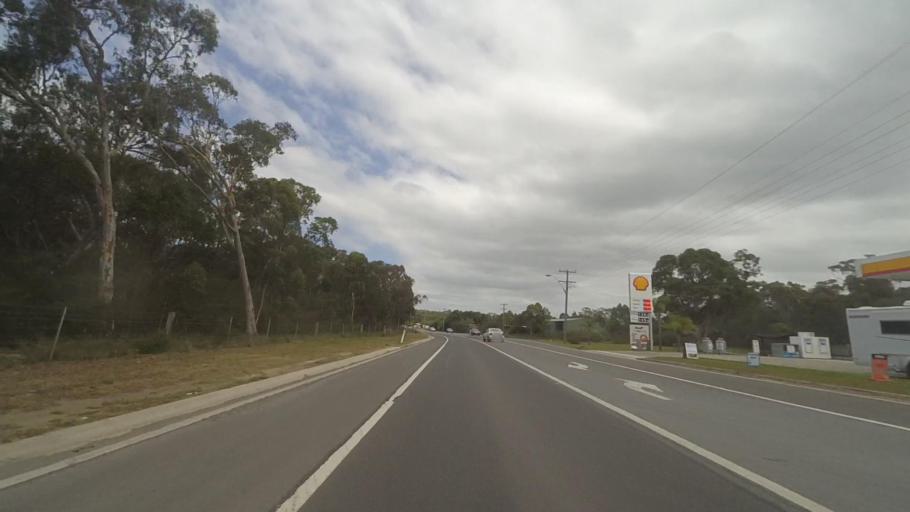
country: AU
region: New South Wales
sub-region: Shoalhaven Shire
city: Falls Creek
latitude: -35.0915
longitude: 150.5079
